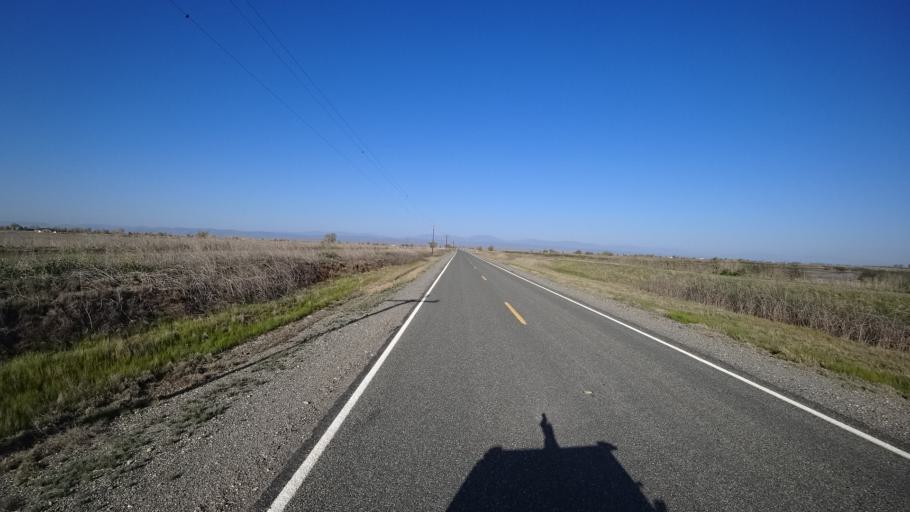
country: US
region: California
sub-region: Glenn County
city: Willows
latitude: 39.4072
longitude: -122.1715
